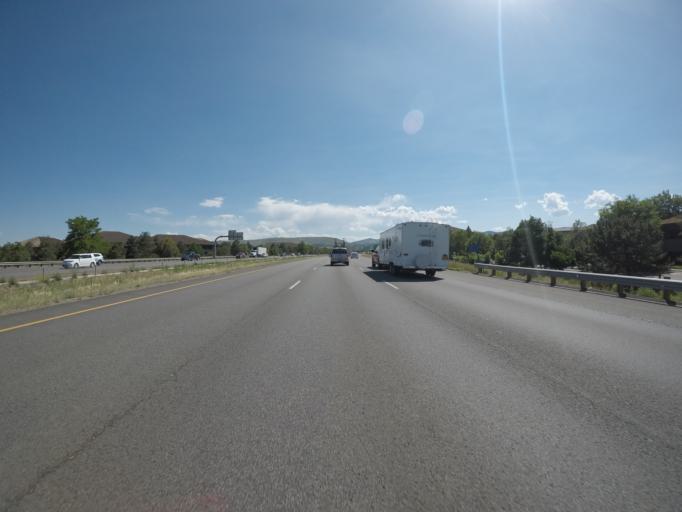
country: US
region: Colorado
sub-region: Jefferson County
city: Applewood
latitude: 39.7461
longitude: -105.1521
